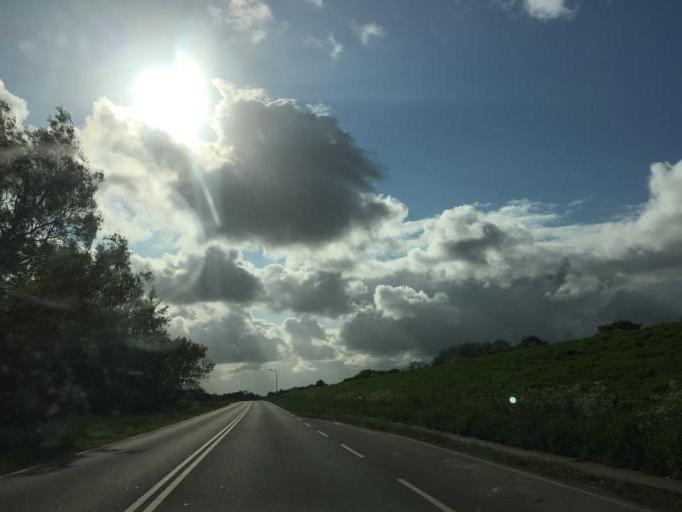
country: NL
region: North Holland
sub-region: Gemeente Opmeer
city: Opmeer
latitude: 52.7523
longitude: 4.9737
